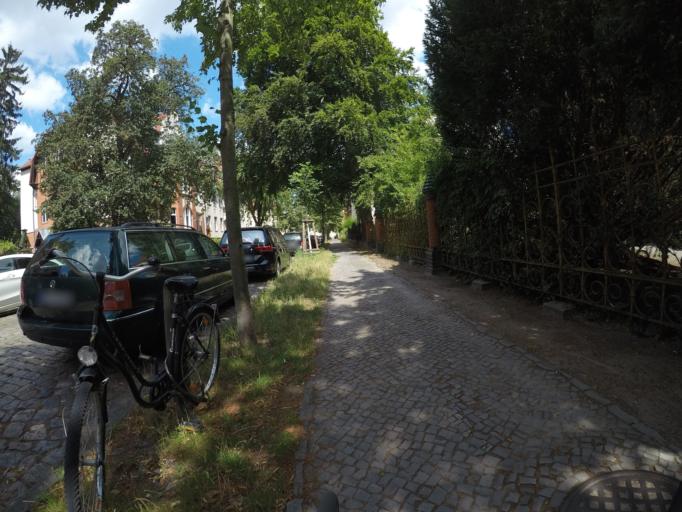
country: DE
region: Brandenburg
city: Potsdam
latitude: 52.3965
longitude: 13.0361
